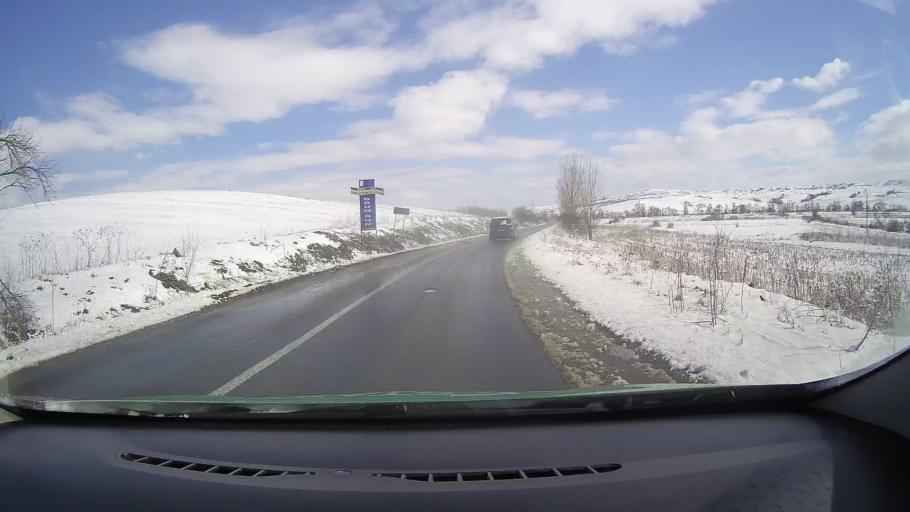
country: RO
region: Sibiu
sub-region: Comuna Nocrich
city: Nocrich
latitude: 45.9019
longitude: 24.4600
